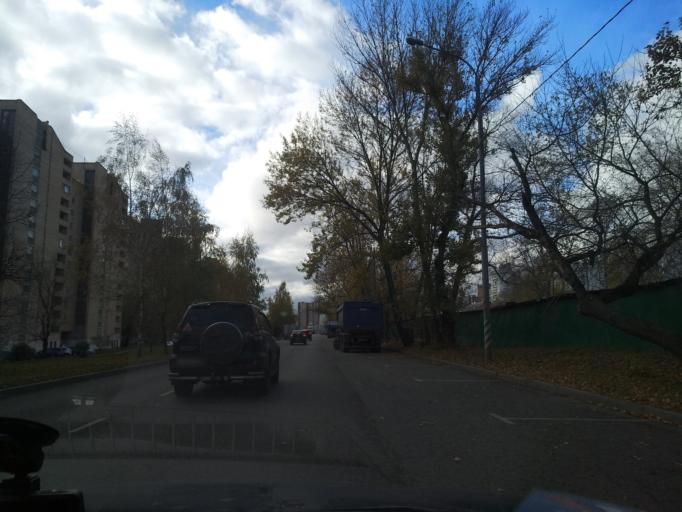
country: RU
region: Moscow
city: Otradnoye
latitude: 55.8735
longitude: 37.6018
